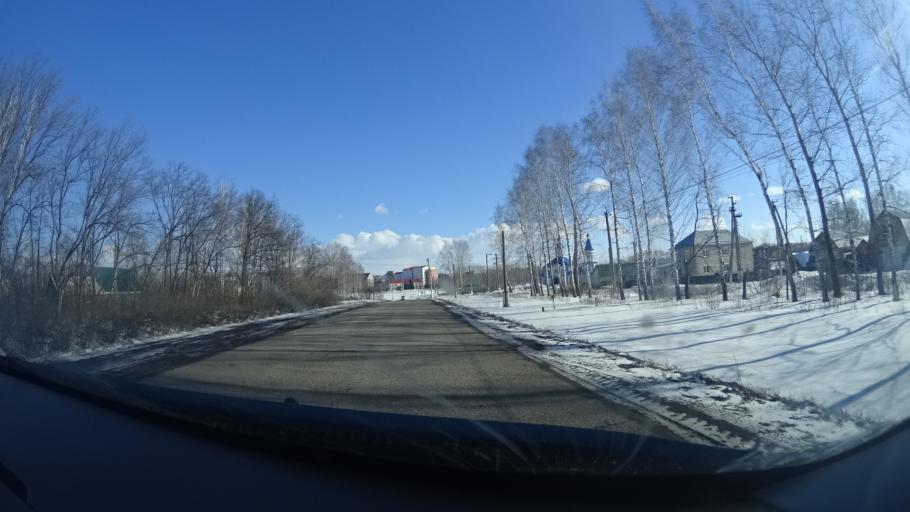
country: RU
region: Bashkortostan
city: Chishmy
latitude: 54.5933
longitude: 55.3634
